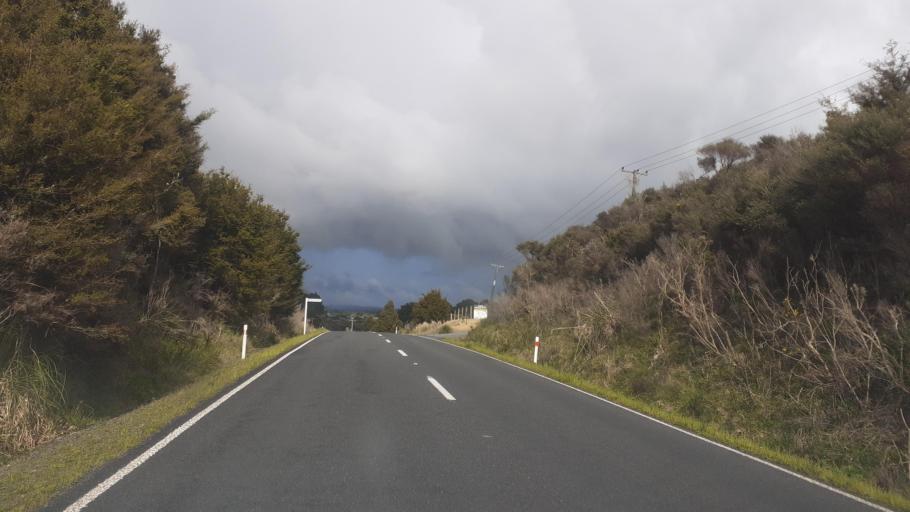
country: NZ
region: Northland
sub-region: Far North District
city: Waimate North
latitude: -35.3095
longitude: 173.7980
